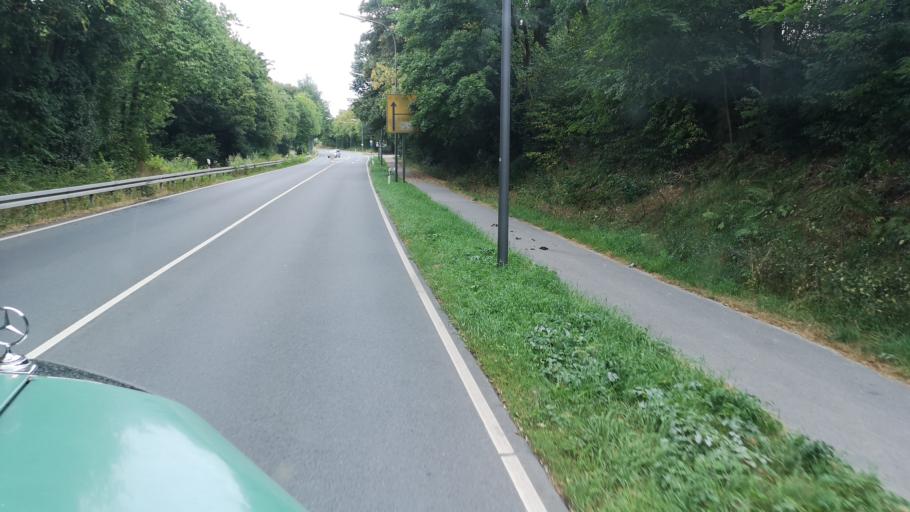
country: DE
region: North Rhine-Westphalia
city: Wermelskirchen
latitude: 51.0961
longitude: 7.1962
